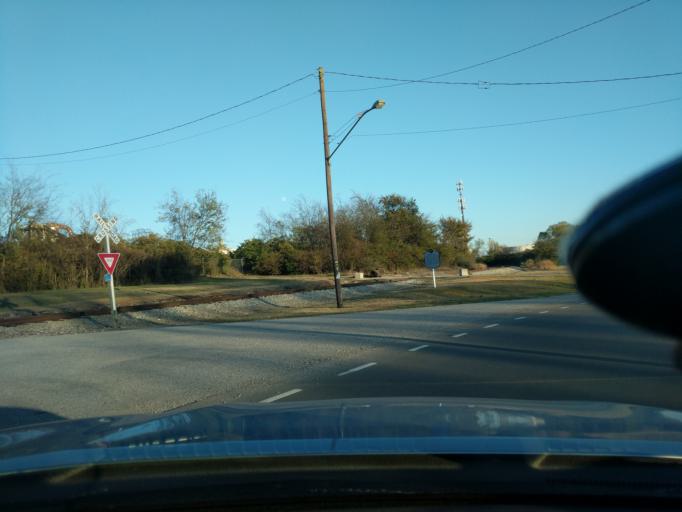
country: US
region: Tennessee
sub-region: Davidson County
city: Belle Meade
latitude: 36.1715
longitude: -86.8631
